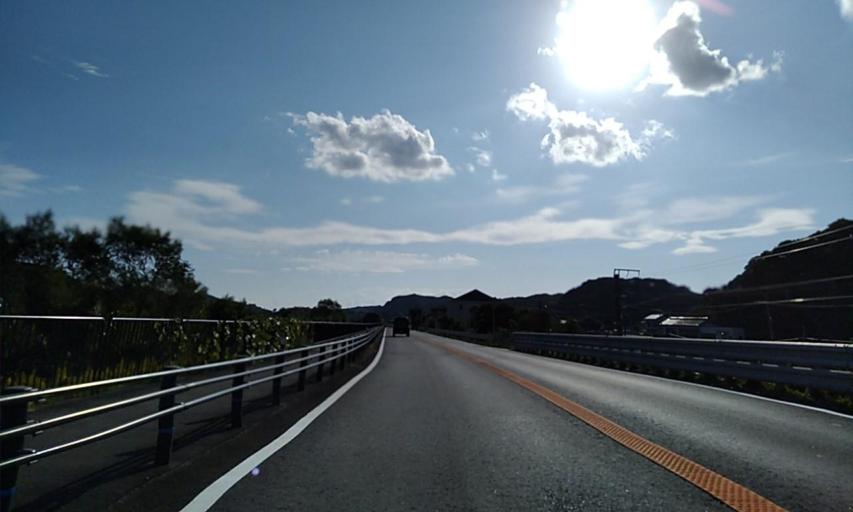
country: JP
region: Wakayama
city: Tanabe
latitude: 33.6849
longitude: 135.4121
